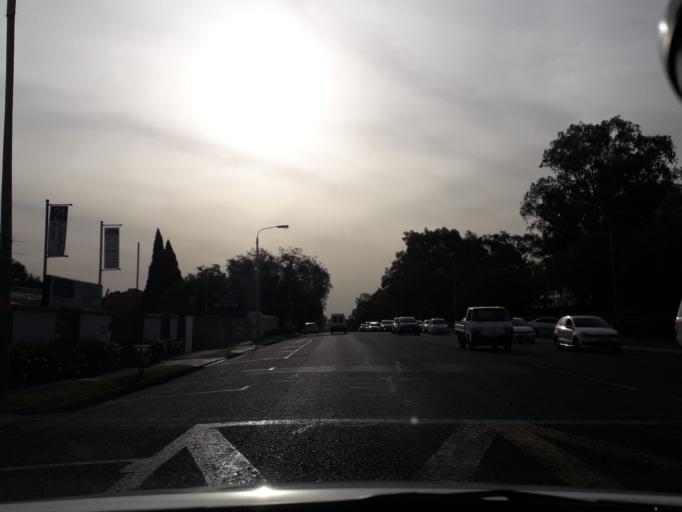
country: ZA
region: Gauteng
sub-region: City of Johannesburg Metropolitan Municipality
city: Modderfontein
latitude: -26.1500
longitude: 28.1472
